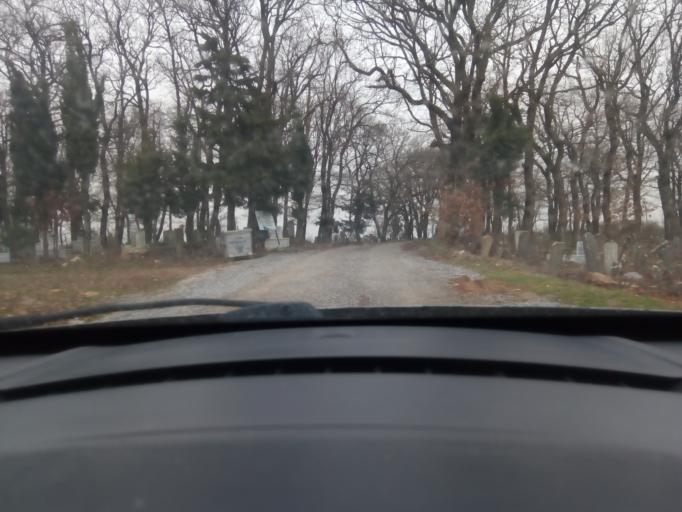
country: TR
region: Balikesir
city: Omerkoy
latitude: 39.8897
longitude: 28.0249
